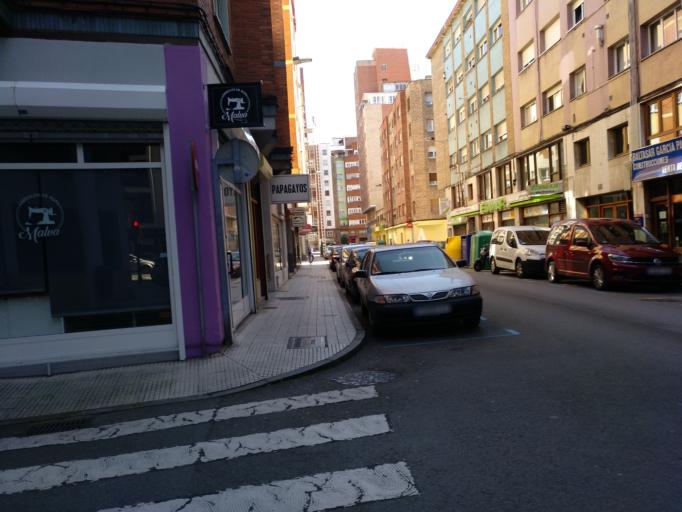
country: ES
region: Asturias
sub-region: Province of Asturias
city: Gijon
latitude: 43.5370
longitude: -5.6680
